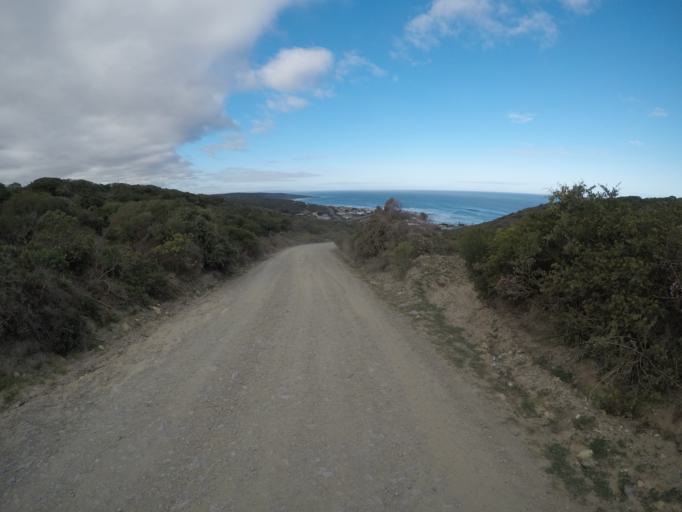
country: ZA
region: Western Cape
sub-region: Eden District Municipality
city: Riversdale
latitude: -34.4241
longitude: 21.3304
